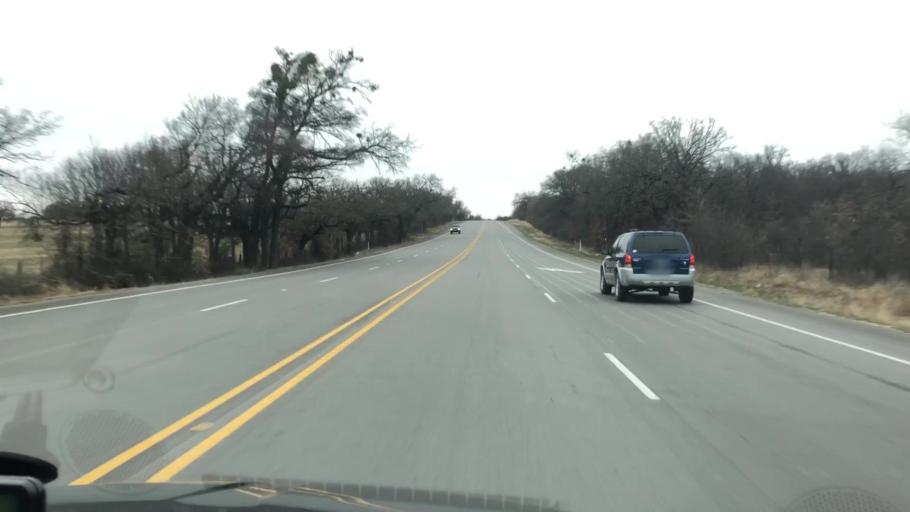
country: US
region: Texas
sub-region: Hamilton County
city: Hico
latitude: 32.0111
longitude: -98.0618
